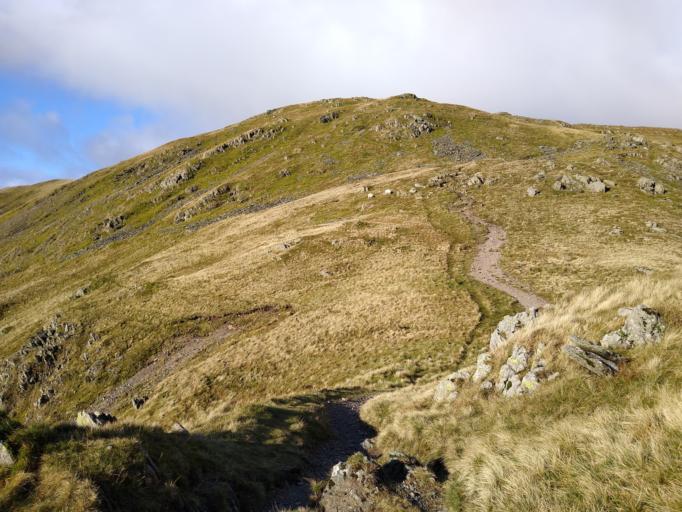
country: GB
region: England
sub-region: Cumbria
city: Windermere
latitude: 54.4784
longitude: -2.8486
